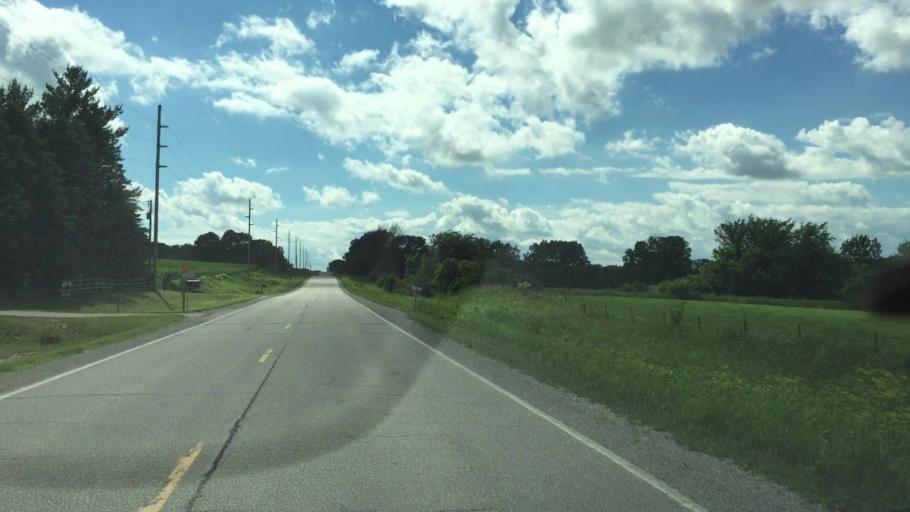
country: US
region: Iowa
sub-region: Linn County
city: Ely
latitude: 41.8474
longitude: -91.5967
